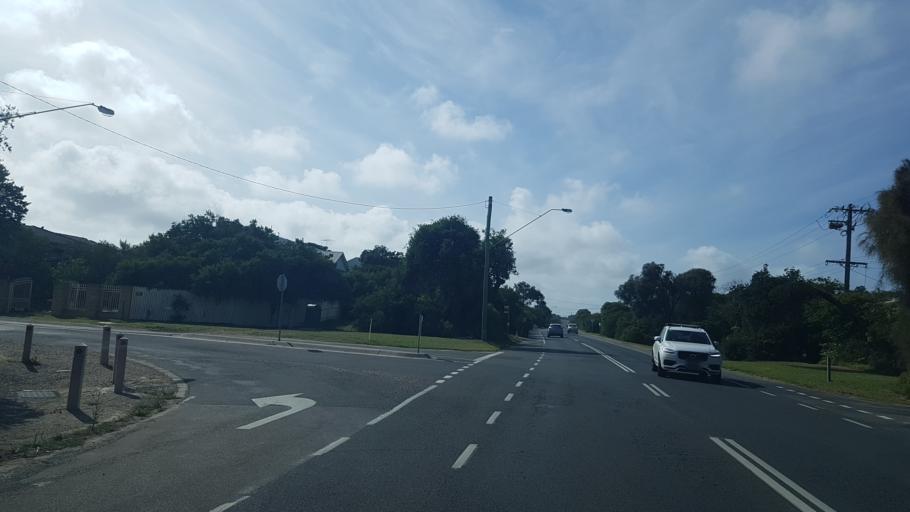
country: AU
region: Victoria
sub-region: Mornington Peninsula
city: Sorrento
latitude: -38.3477
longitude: 144.7420
